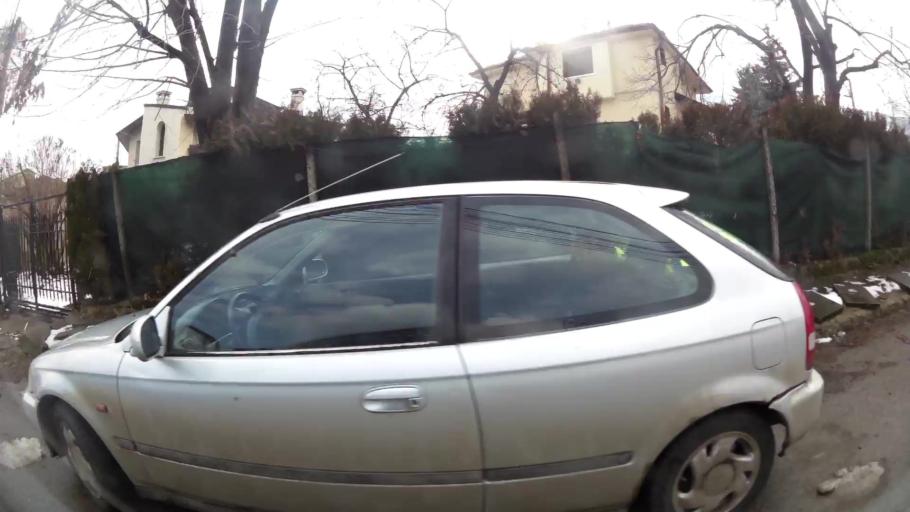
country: BG
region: Sofia-Capital
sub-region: Stolichna Obshtina
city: Sofia
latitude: 42.6466
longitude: 23.2798
